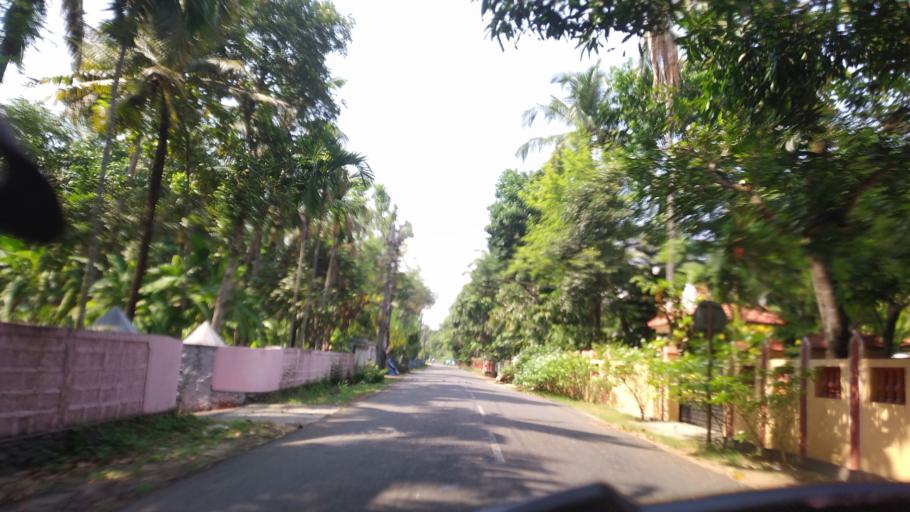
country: IN
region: Kerala
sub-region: Thrissur District
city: Irinjalakuda
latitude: 10.3077
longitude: 76.1285
